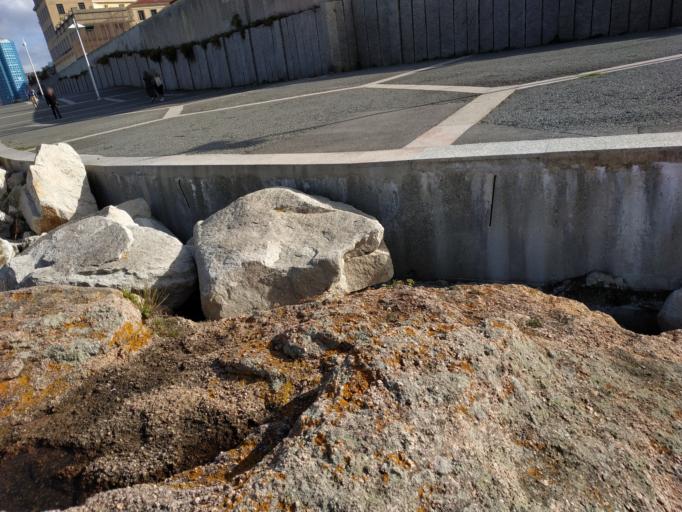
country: ES
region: Galicia
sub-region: Provincia da Coruna
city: A Coruna
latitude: 43.3713
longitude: -8.4163
